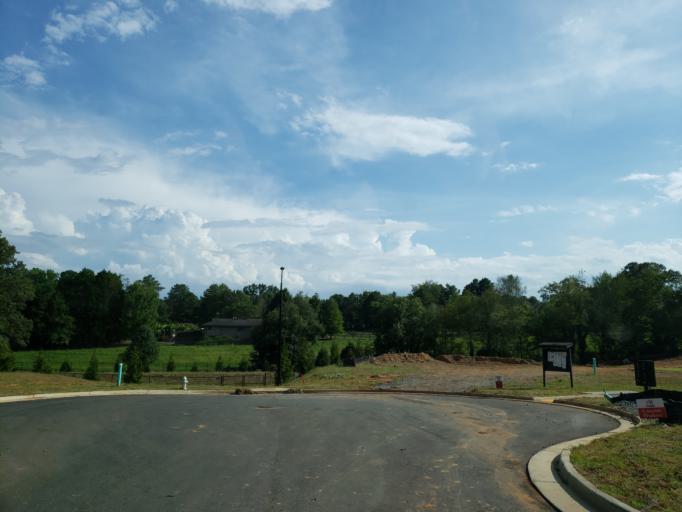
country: US
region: Georgia
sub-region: Cherokee County
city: Woodstock
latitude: 34.0433
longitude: -84.5099
